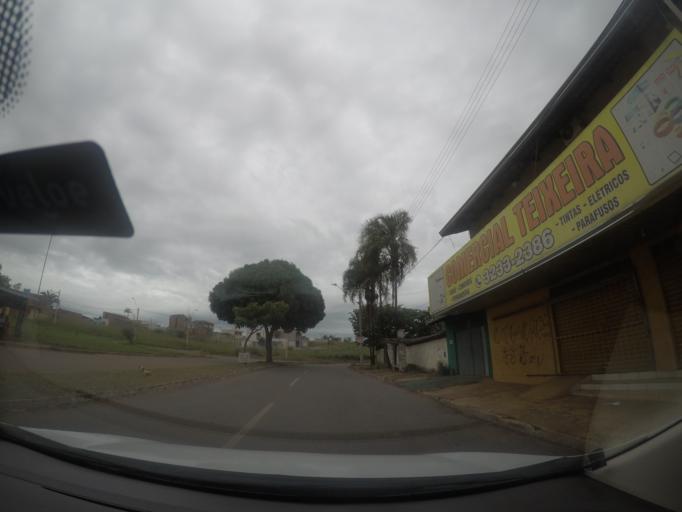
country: BR
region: Goias
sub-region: Goiania
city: Goiania
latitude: -16.6178
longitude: -49.3041
